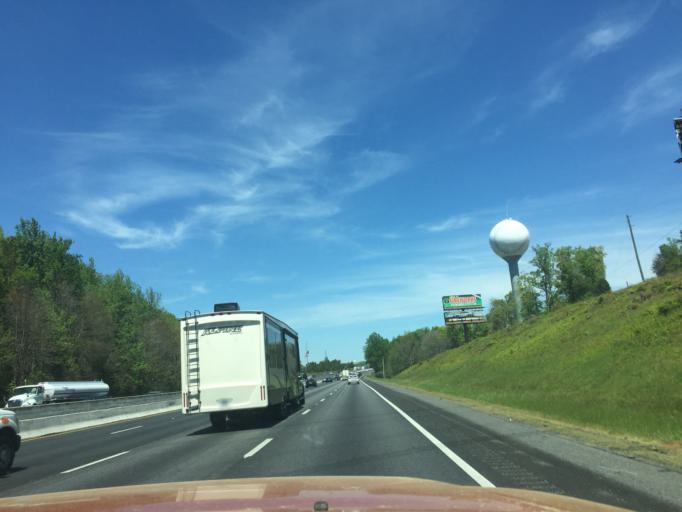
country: US
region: South Carolina
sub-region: York County
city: Fort Mill
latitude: 35.0526
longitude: -80.9582
